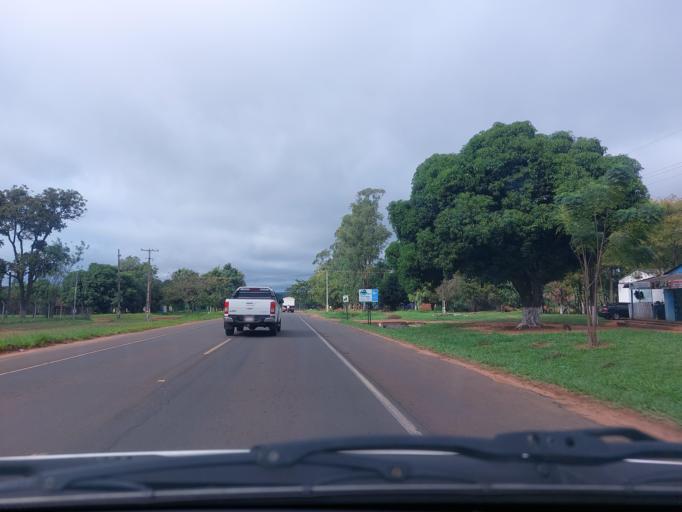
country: PY
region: San Pedro
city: Guayaybi
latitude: -24.6207
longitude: -56.3804
